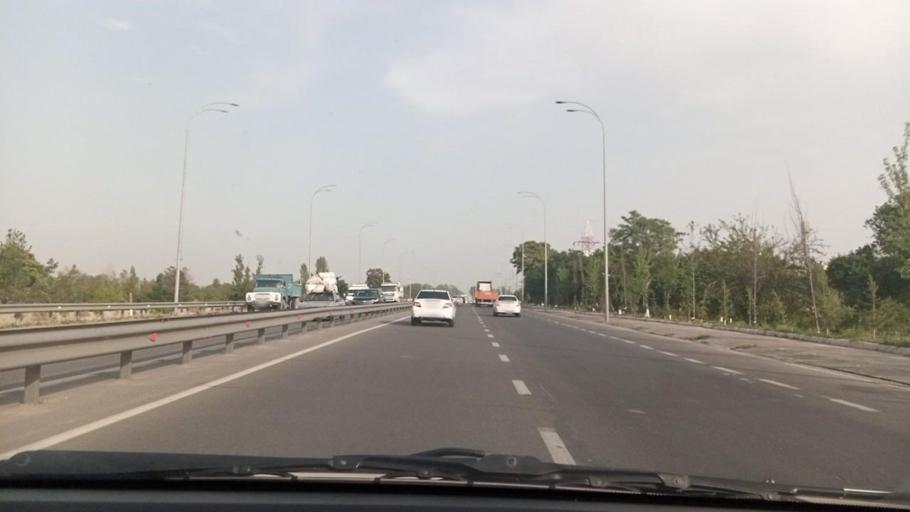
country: UZ
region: Toshkent Shahri
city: Bektemir
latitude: 41.2605
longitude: 69.3760
